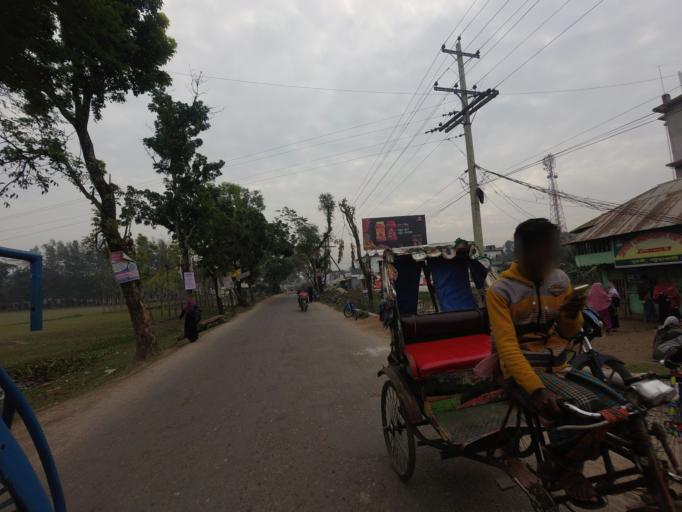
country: BD
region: Barisal
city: Nalchiti
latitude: 22.4650
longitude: 90.3770
